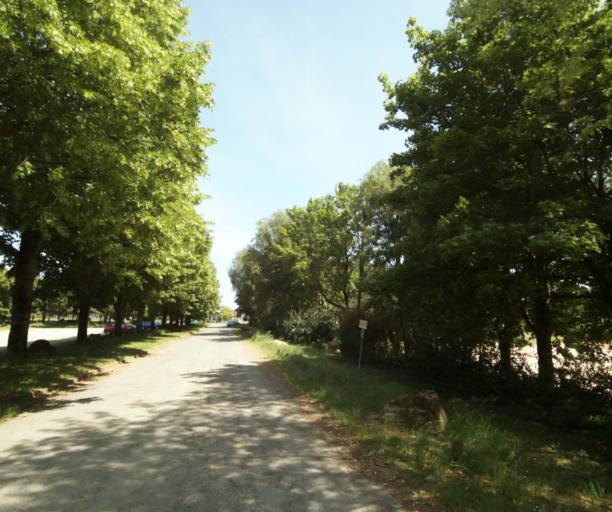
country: FR
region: Champagne-Ardenne
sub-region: Departement des Ardennes
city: Prix-les-Mezieres
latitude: 49.7605
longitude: 4.6844
